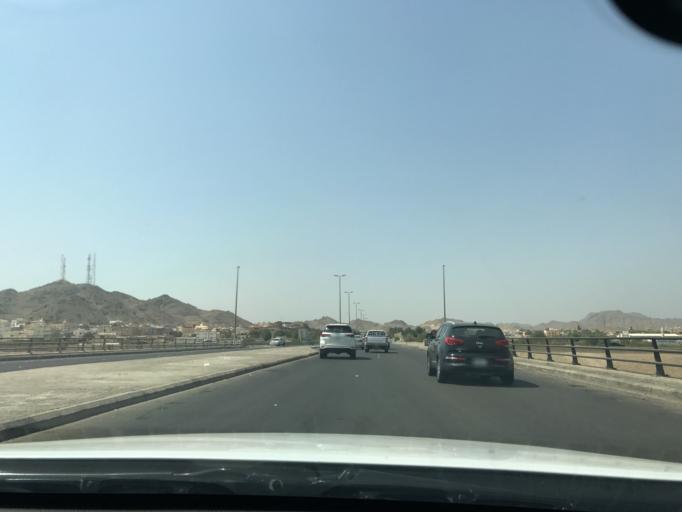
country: SA
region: Makkah
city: Jeddah
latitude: 21.3886
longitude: 39.4270
